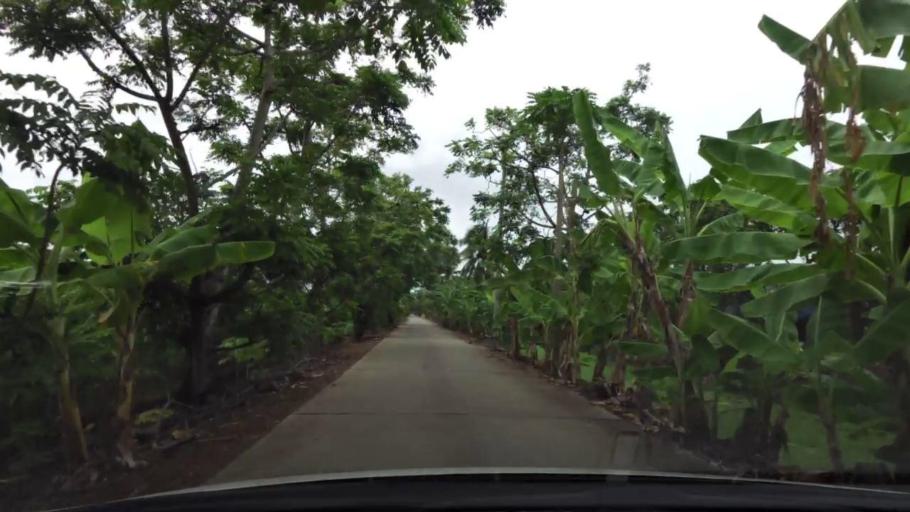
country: TH
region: Ratchaburi
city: Damnoen Saduak
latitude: 13.5585
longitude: 100.0061
